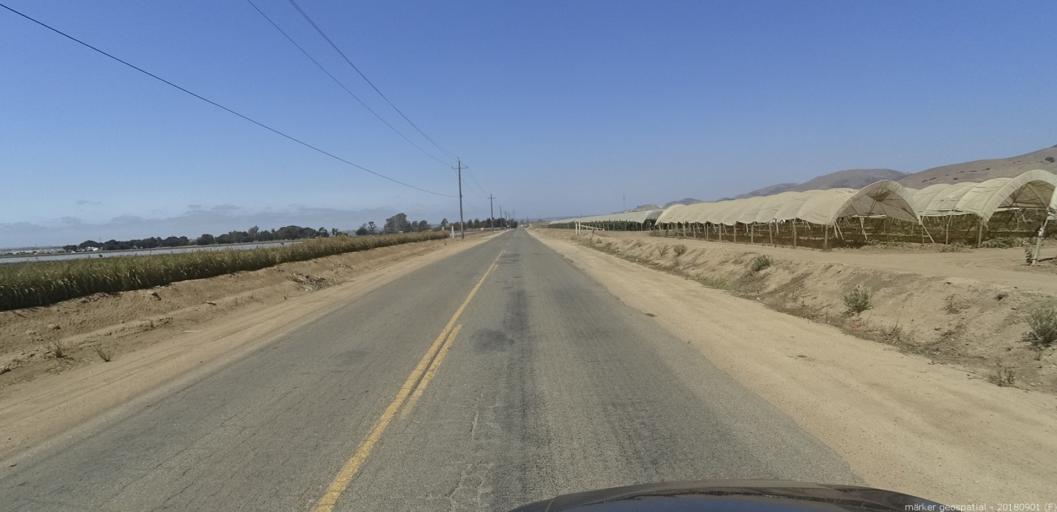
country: US
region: California
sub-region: Monterey County
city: Salinas
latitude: 36.6947
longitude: -121.5708
